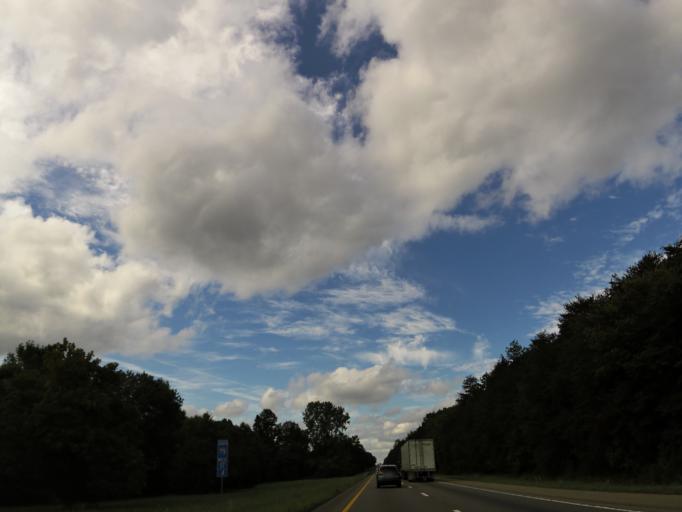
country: US
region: Tennessee
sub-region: Monroe County
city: Sweetwater
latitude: 35.5645
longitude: -84.5501
